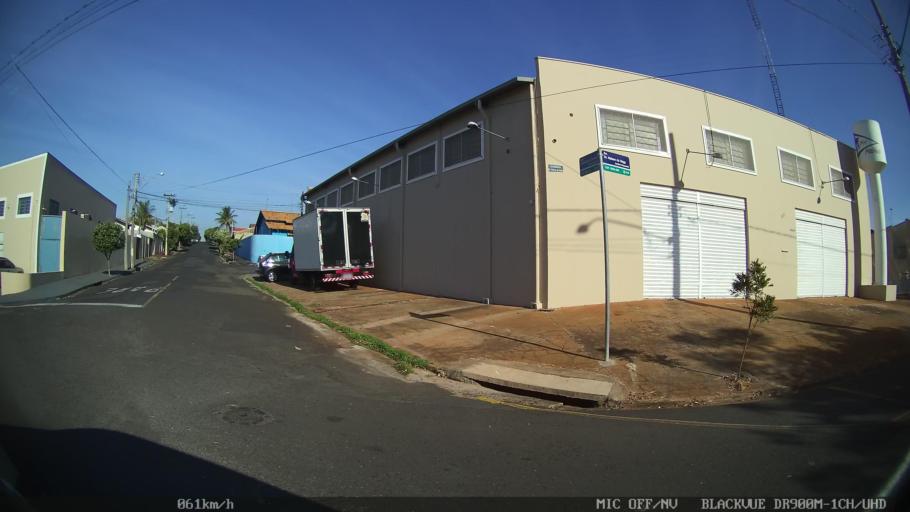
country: BR
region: Sao Paulo
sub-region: Sao Jose Do Rio Preto
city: Sao Jose do Rio Preto
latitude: -20.7796
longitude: -49.3598
